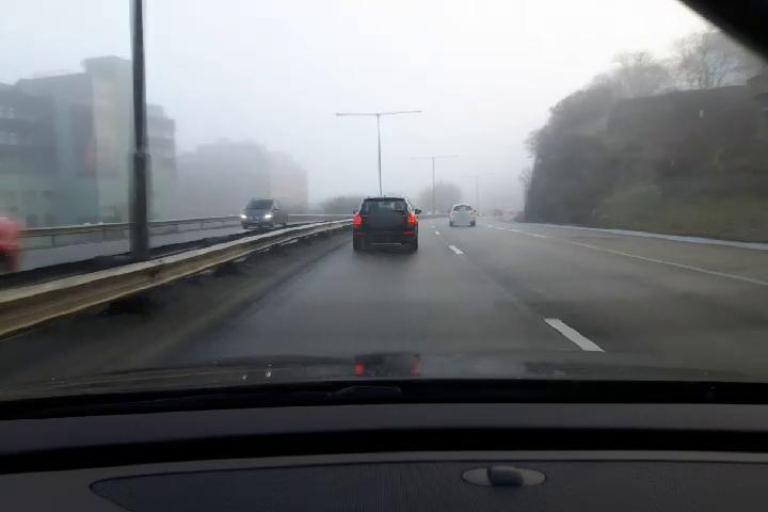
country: SE
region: Vaestra Goetaland
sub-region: Goteborg
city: Majorna
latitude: 57.6989
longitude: 11.9301
